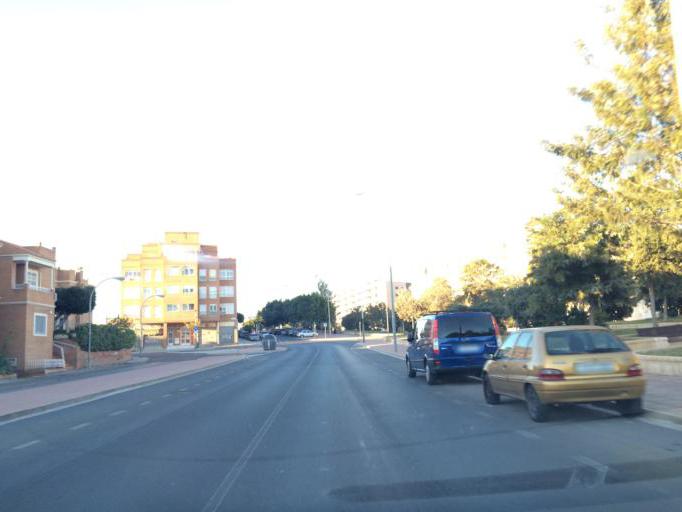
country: ES
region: Andalusia
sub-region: Provincia de Almeria
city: Almeria
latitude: 36.8526
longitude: -2.4393
